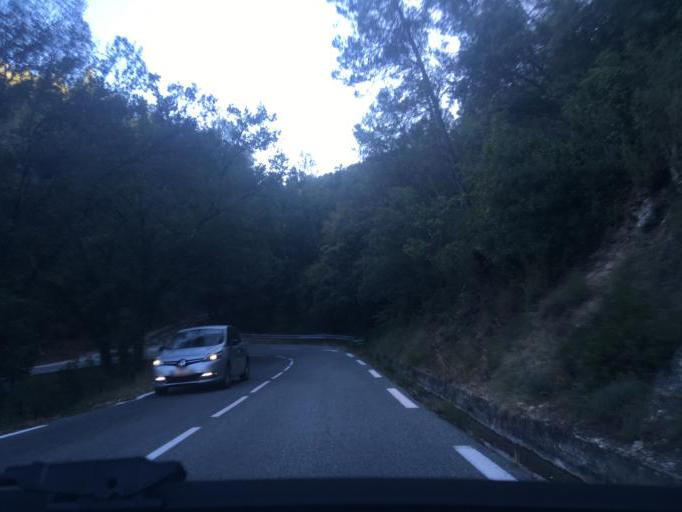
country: FR
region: Provence-Alpes-Cote d'Azur
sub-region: Departement du Var
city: Flayosc
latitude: 43.5631
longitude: 6.4166
